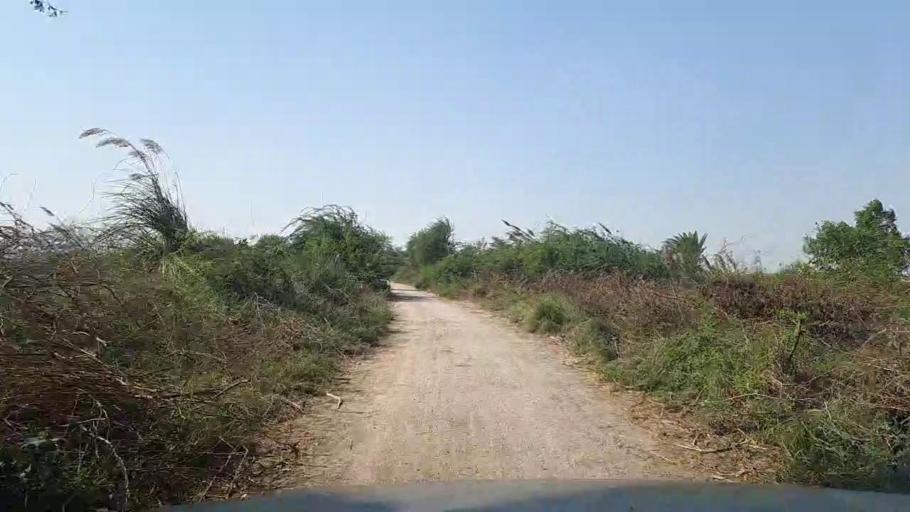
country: PK
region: Sindh
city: Mirpur Batoro
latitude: 24.6947
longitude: 68.1668
